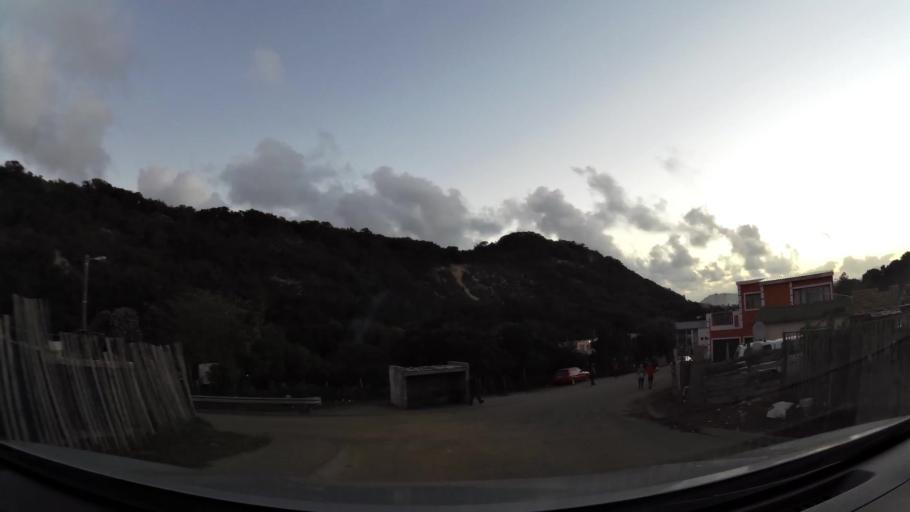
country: ZA
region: Western Cape
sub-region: Eden District Municipality
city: Knysna
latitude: -34.0274
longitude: 22.8212
